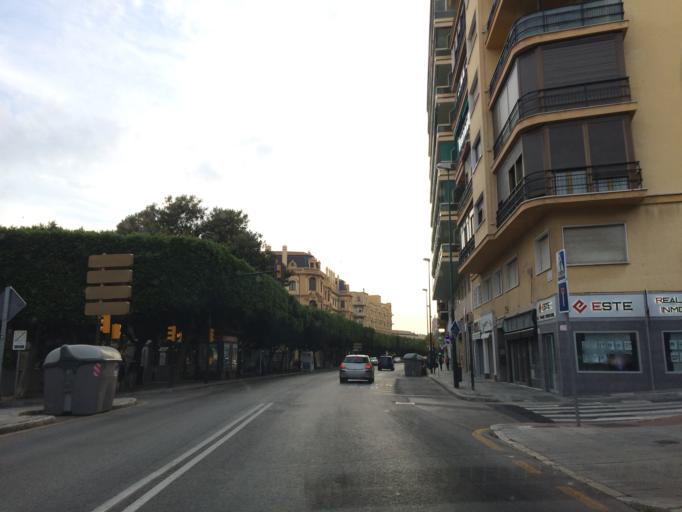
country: ES
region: Andalusia
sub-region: Provincia de Malaga
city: Malaga
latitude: 36.7211
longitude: -4.4070
